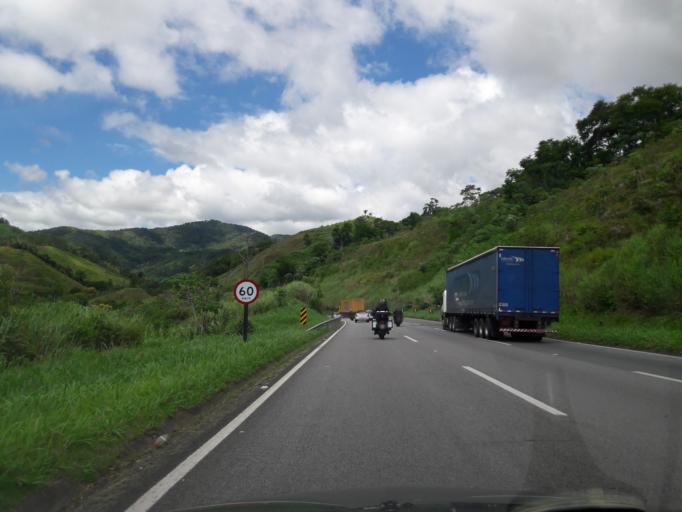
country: BR
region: Sao Paulo
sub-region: Cajati
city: Cajati
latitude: -24.8313
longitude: -48.2212
